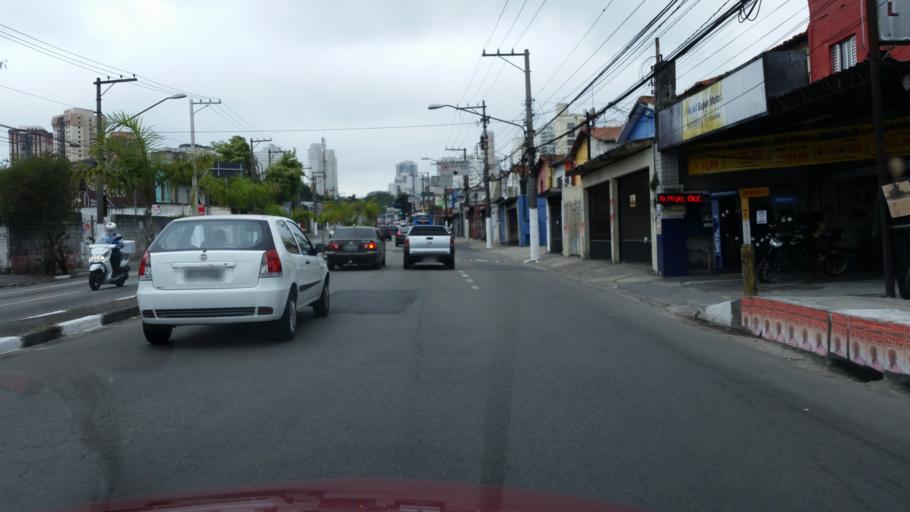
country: BR
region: Sao Paulo
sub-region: Diadema
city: Diadema
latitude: -23.6597
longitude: -46.7008
